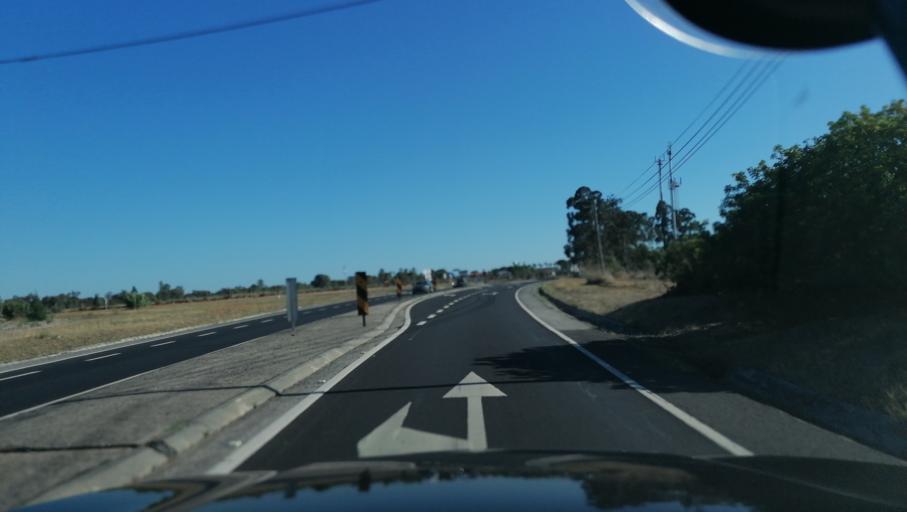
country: PT
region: Setubal
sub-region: Alcochete
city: Alcochete
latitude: 38.7843
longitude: -8.8807
